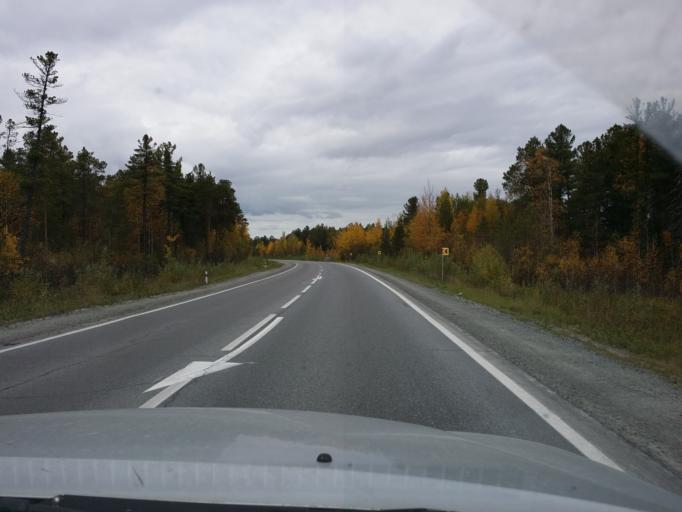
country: RU
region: Khanty-Mansiyskiy Avtonomnyy Okrug
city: Langepas
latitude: 61.2237
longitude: 75.3306
